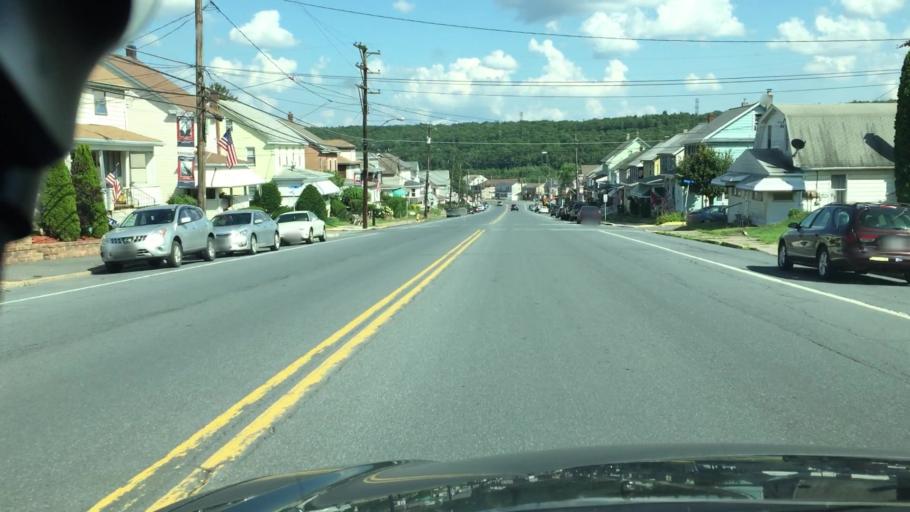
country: US
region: Pennsylvania
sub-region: Luzerne County
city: Oakdale
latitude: 40.9304
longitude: -75.9187
